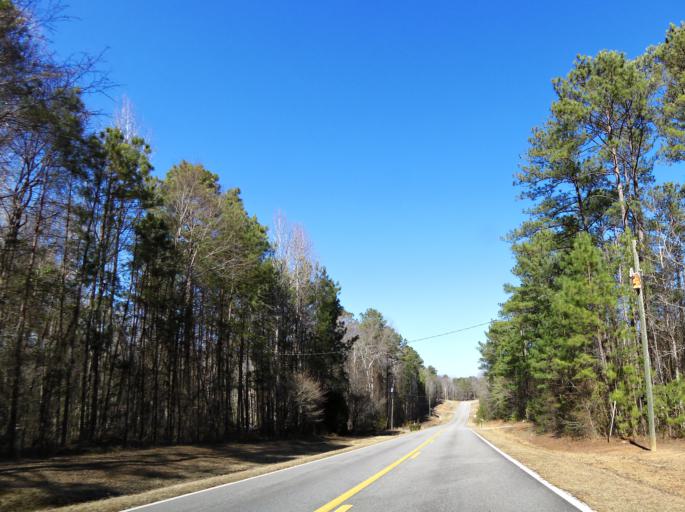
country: US
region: Georgia
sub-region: Bibb County
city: West Point
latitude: 32.8205
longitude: -83.8417
